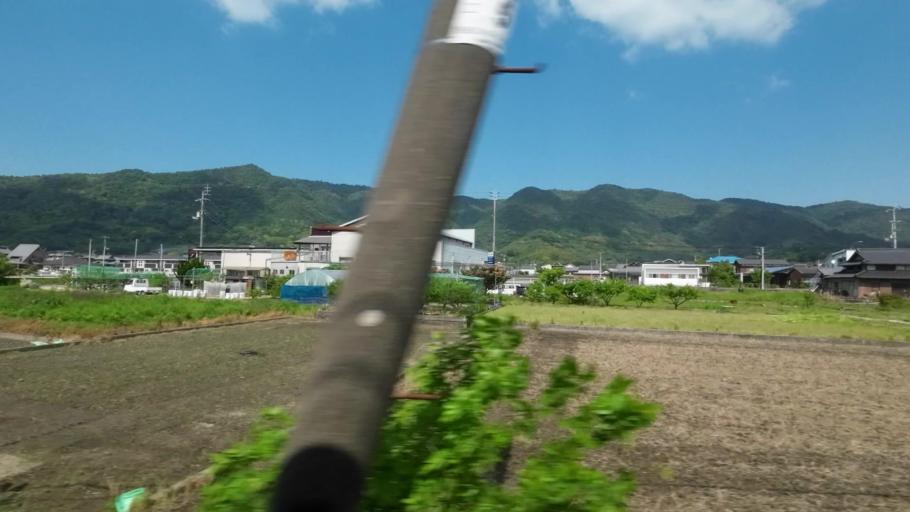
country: JP
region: Kagawa
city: Kan'onjicho
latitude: 34.1634
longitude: 133.6897
